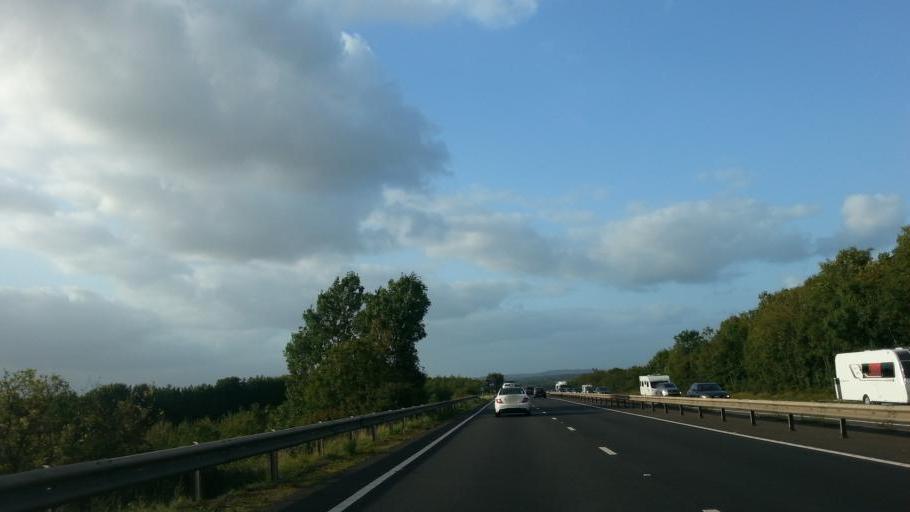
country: GB
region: England
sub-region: Hampshire
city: Overton
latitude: 51.2095
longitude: -1.3404
